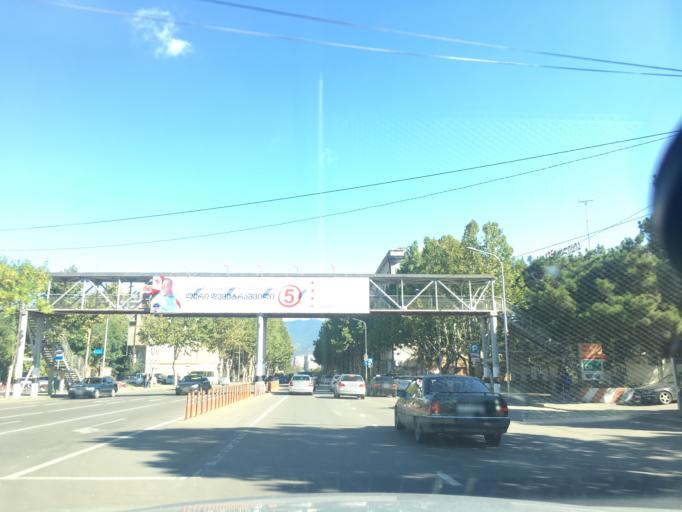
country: GE
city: Zahesi
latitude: 41.7696
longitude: 44.7925
